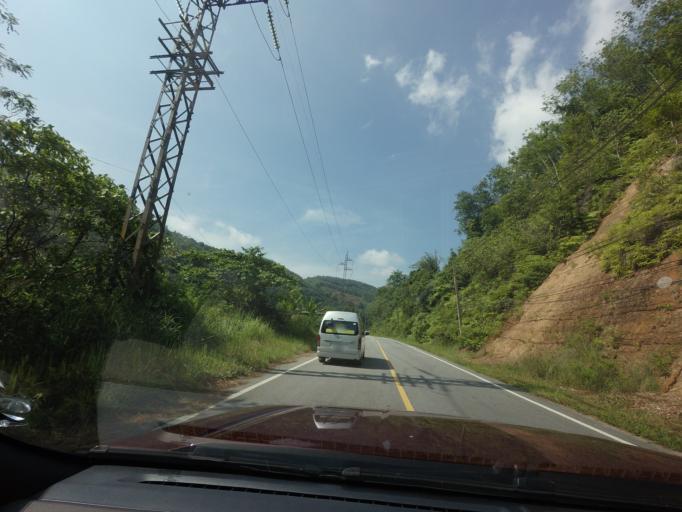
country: TH
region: Yala
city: Betong
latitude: 5.9303
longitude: 101.1862
